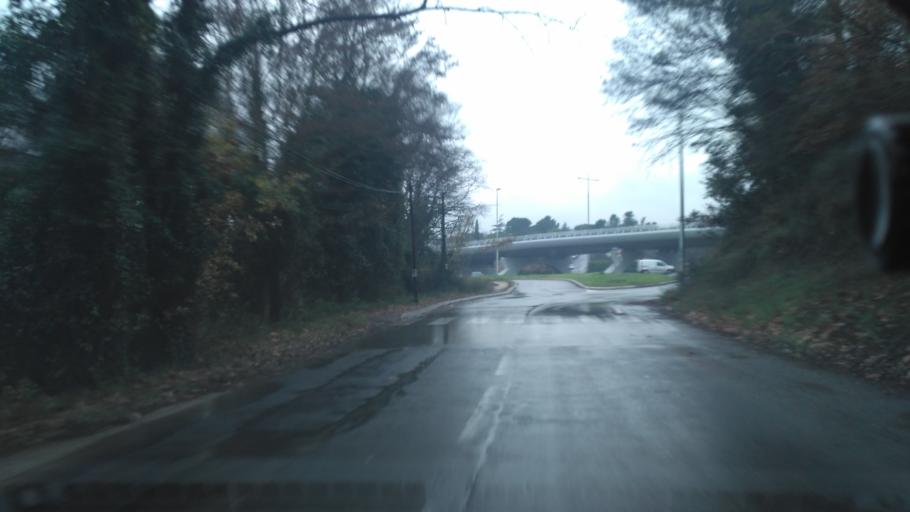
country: FR
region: Languedoc-Roussillon
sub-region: Departement de l'Herault
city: Montferrier-sur-Lez
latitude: 43.6498
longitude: 3.8671
